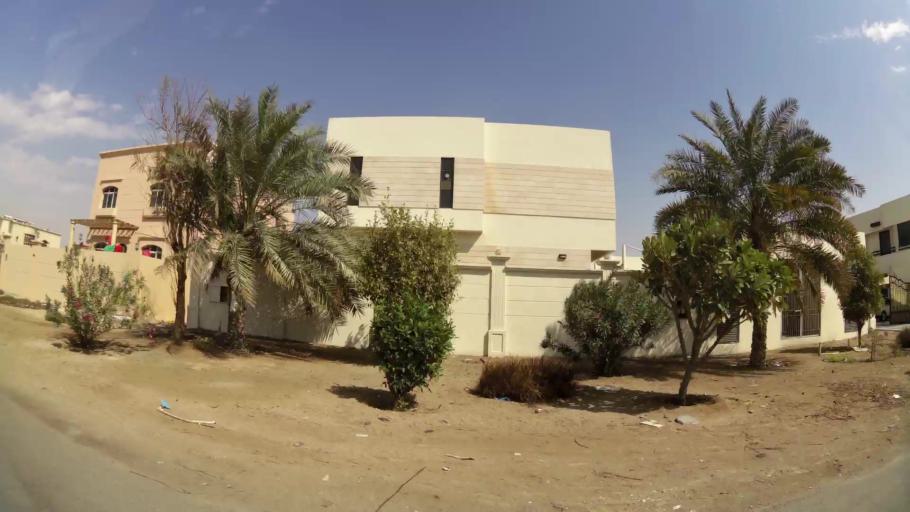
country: AE
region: Abu Dhabi
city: Abu Dhabi
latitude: 24.3275
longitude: 54.5461
